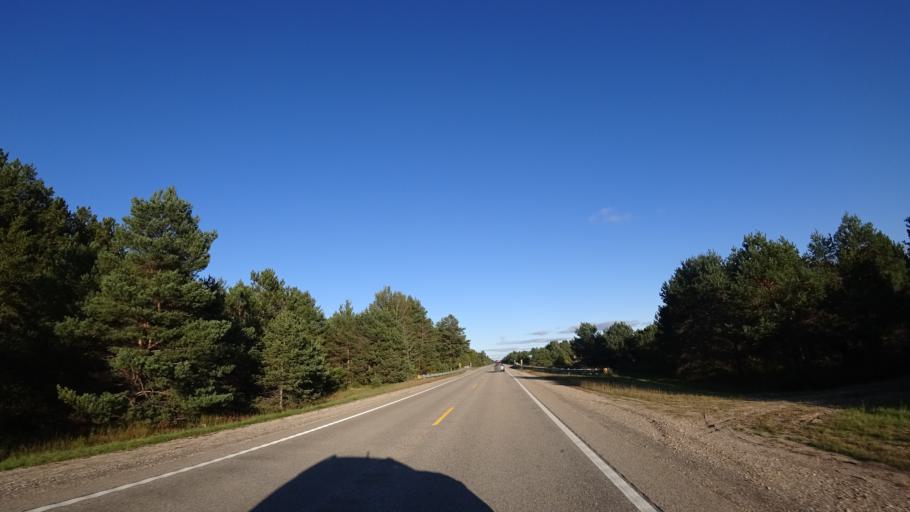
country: US
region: Michigan
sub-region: Schoolcraft County
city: Manistique
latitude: 46.3450
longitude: -85.9919
